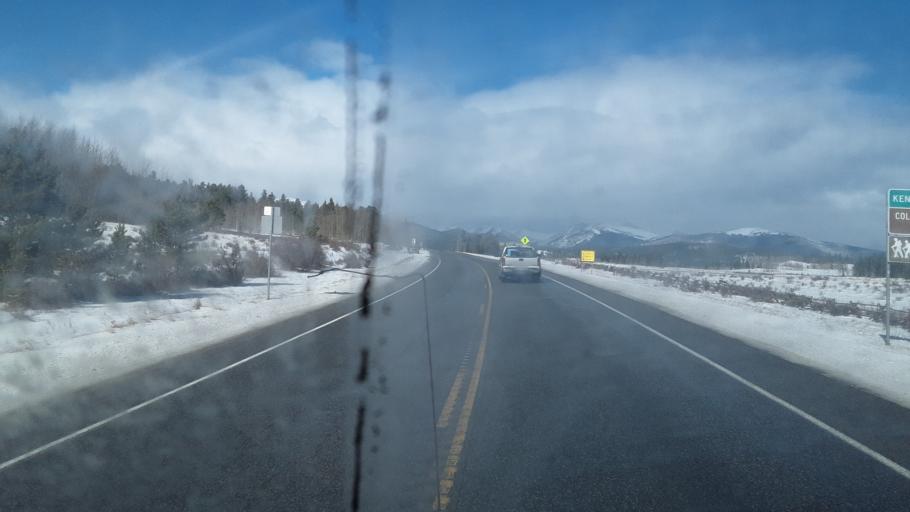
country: US
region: Colorado
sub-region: Summit County
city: Breckenridge
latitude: 39.4113
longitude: -105.7572
